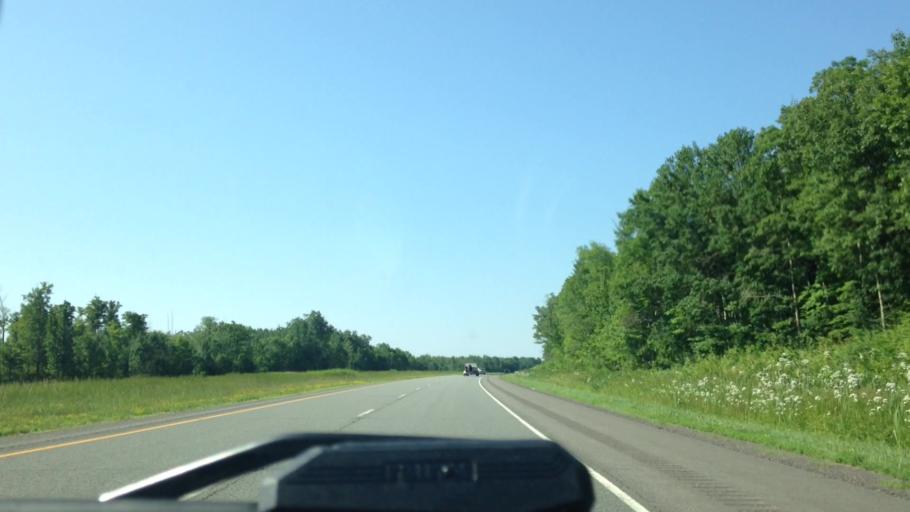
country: US
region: Wisconsin
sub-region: Douglas County
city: Lake Nebagamon
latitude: 46.4142
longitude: -91.8106
